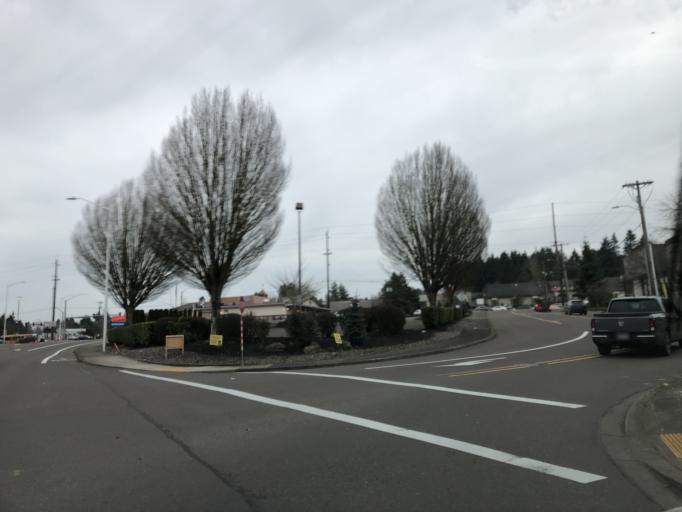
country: US
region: Oregon
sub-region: Washington County
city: King City
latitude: 45.4187
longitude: -122.7897
